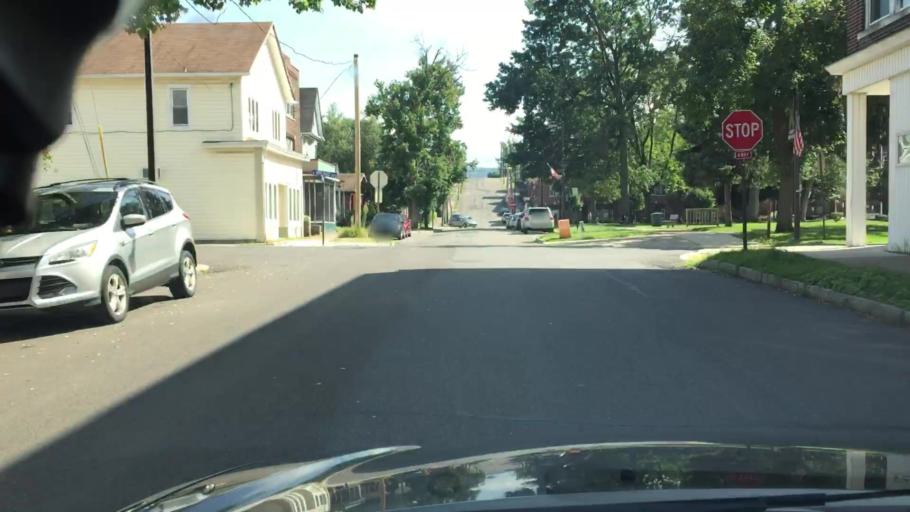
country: US
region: Pennsylvania
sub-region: Luzerne County
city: Nanticoke
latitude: 41.2031
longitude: -76.0025
